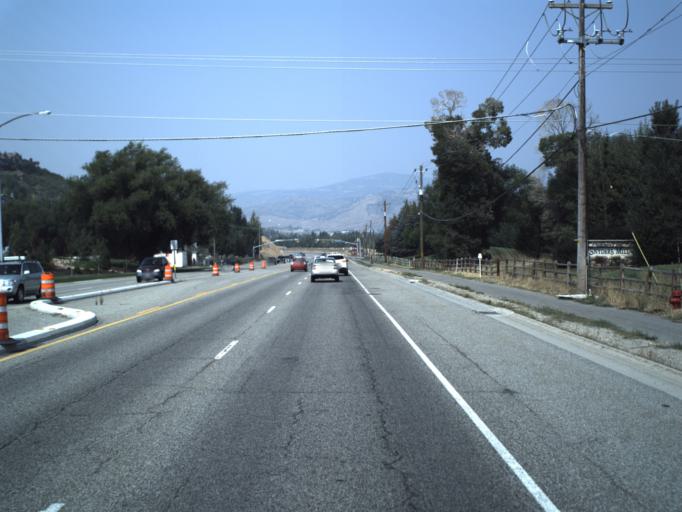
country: US
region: Utah
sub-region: Summit County
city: Snyderville
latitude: 40.6937
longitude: -111.5441
